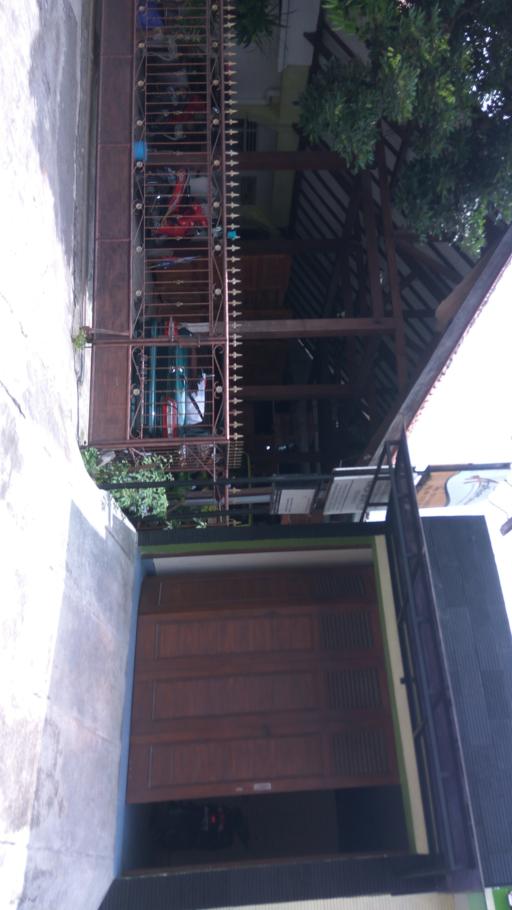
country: ID
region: Daerah Istimewa Yogyakarta
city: Melati
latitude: -7.7201
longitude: 110.4041
